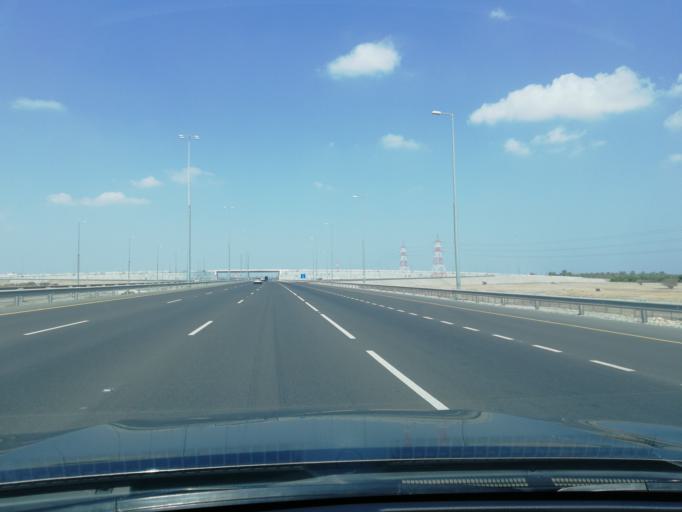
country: OM
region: Al Batinah
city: Barka'
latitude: 23.6309
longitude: 57.9949
